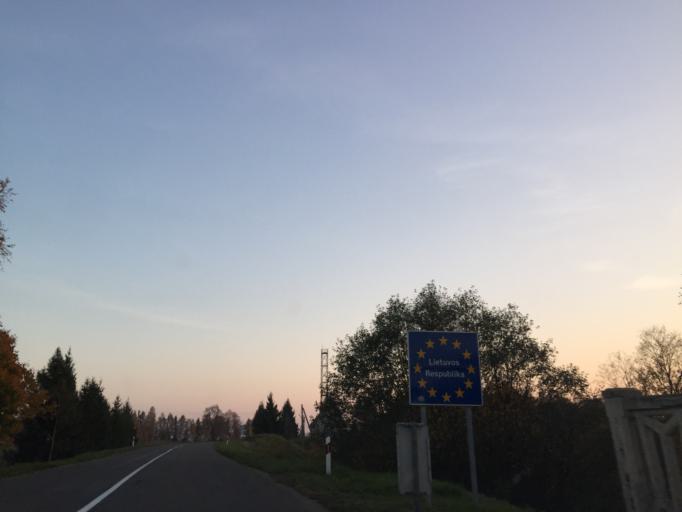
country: LT
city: Skuodas
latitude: 56.2960
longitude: 21.5390
